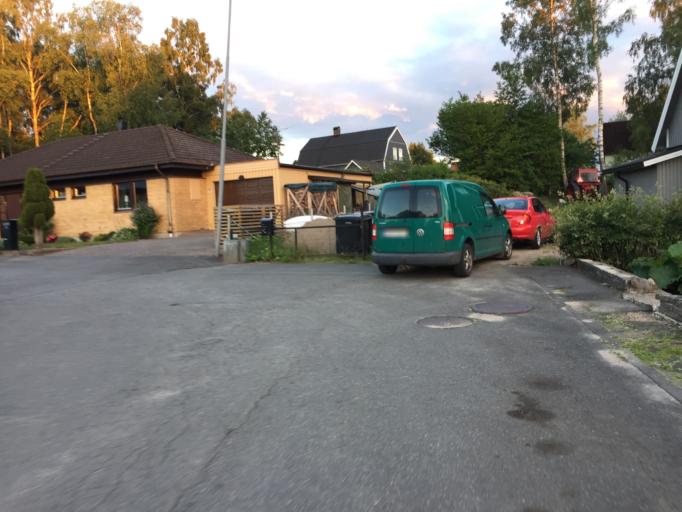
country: SE
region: Skane
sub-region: Hassleholms Kommun
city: Sosdala
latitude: 56.0457
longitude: 13.6817
